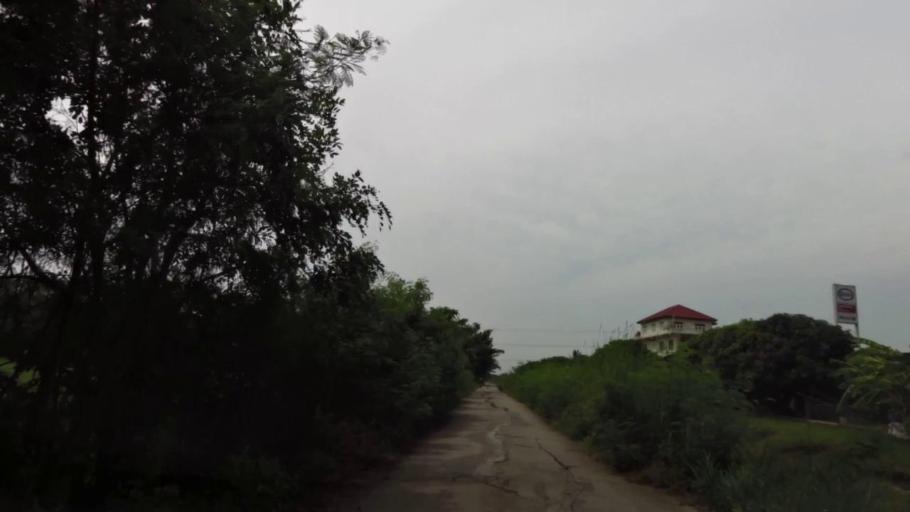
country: TH
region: Lop Buri
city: Ban Mi
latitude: 15.0462
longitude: 100.5614
